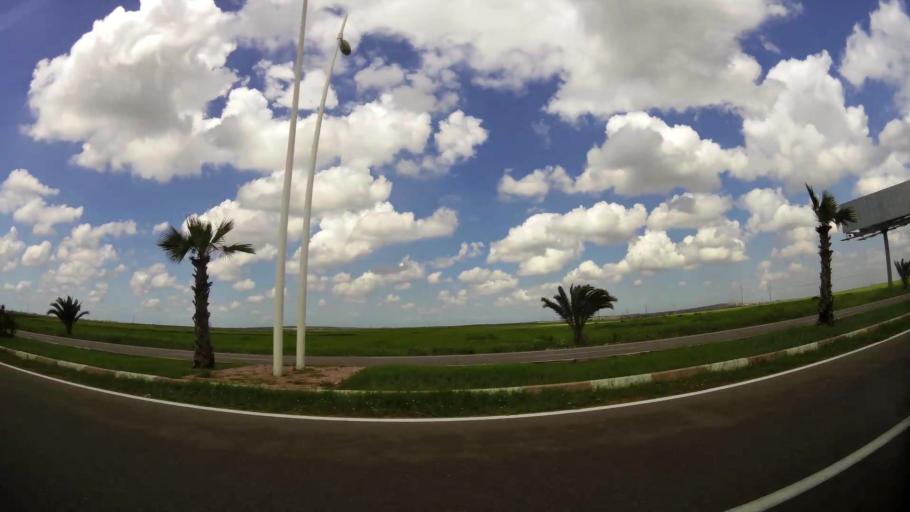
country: MA
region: Chaouia-Ouardigha
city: Nouaseur
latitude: 33.3999
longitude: -7.5746
